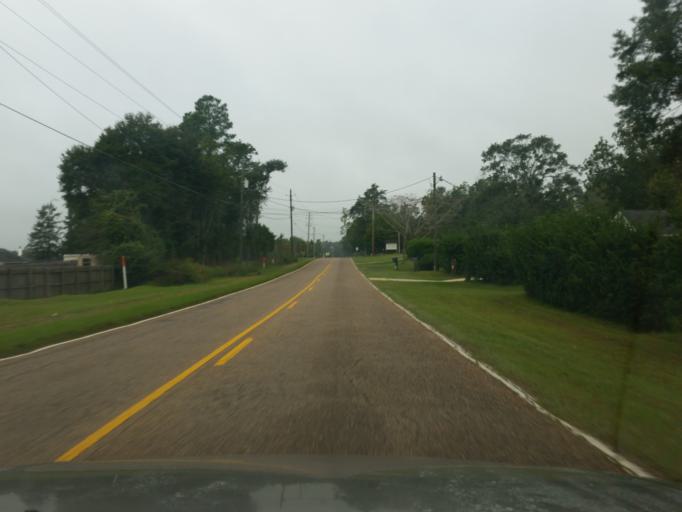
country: US
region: Florida
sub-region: Escambia County
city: Cantonment
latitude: 30.6057
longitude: -87.3467
